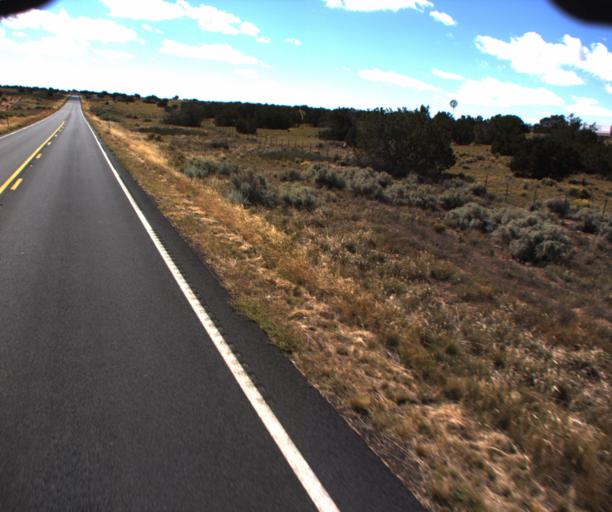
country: US
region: Arizona
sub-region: Apache County
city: Houck
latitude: 35.1422
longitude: -109.3328
